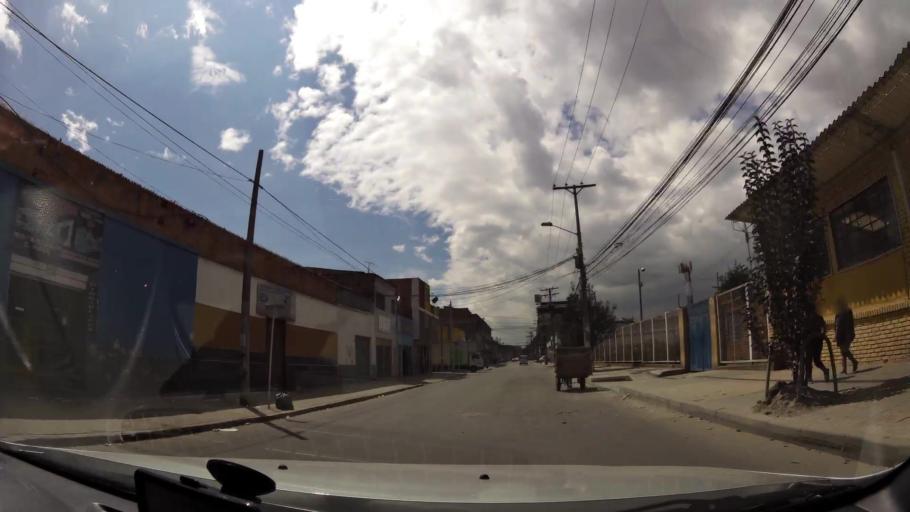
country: CO
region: Bogota D.C.
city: Bogota
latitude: 4.6326
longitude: -74.1086
